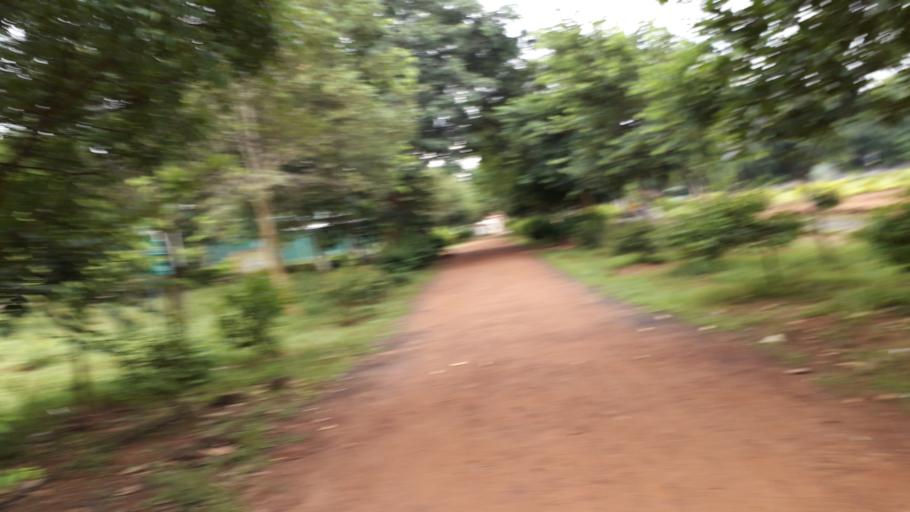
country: IN
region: Andhra Pradesh
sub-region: East Godavari
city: Rajahmundry
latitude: 17.0352
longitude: 81.8256
